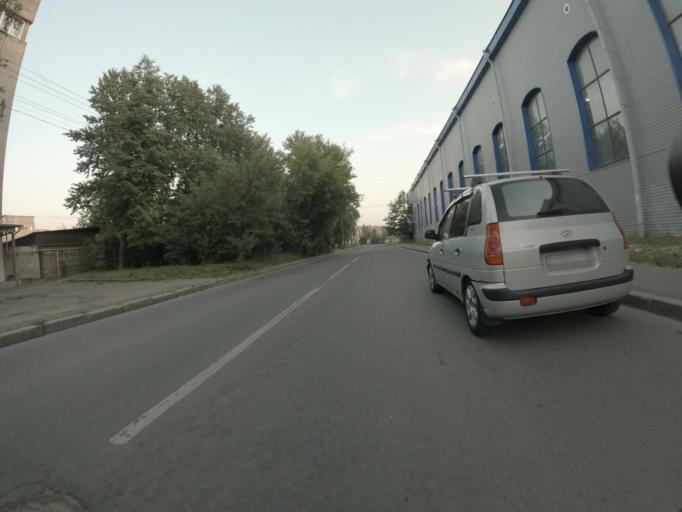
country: RU
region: St.-Petersburg
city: Kupchino
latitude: 59.8901
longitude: 30.3365
